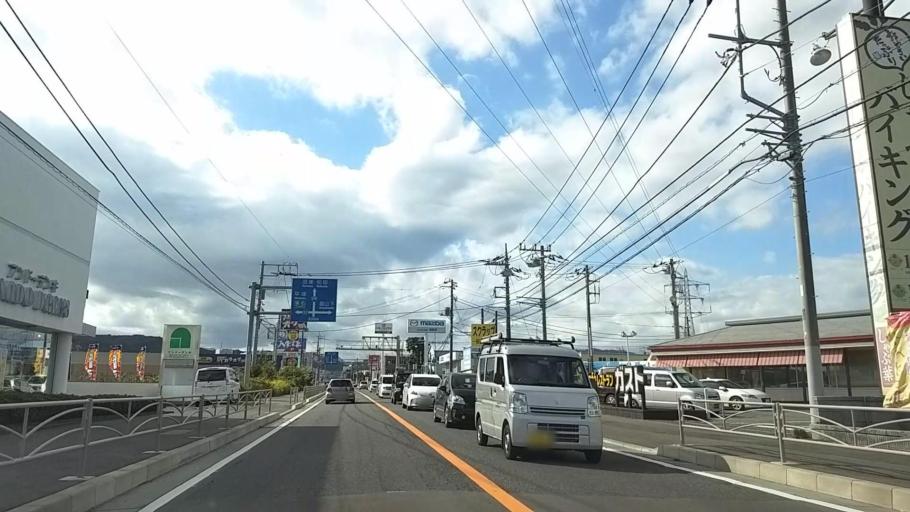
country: JP
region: Kanagawa
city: Hadano
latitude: 35.3750
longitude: 139.2047
